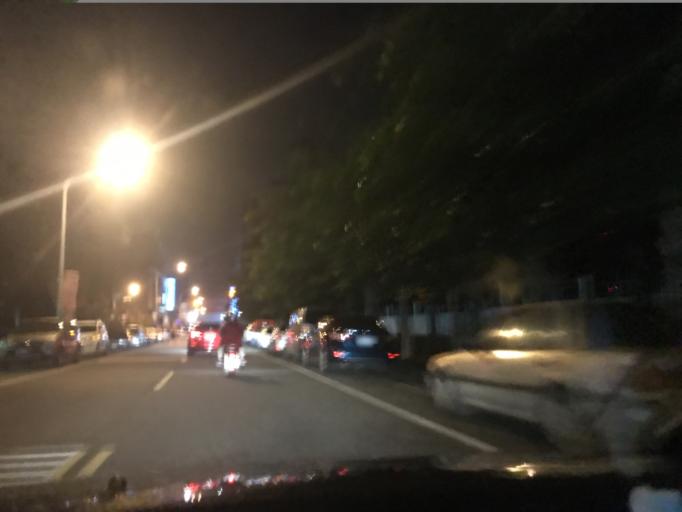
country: TW
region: Taiwan
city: Taoyuan City
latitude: 24.9494
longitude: 121.2096
